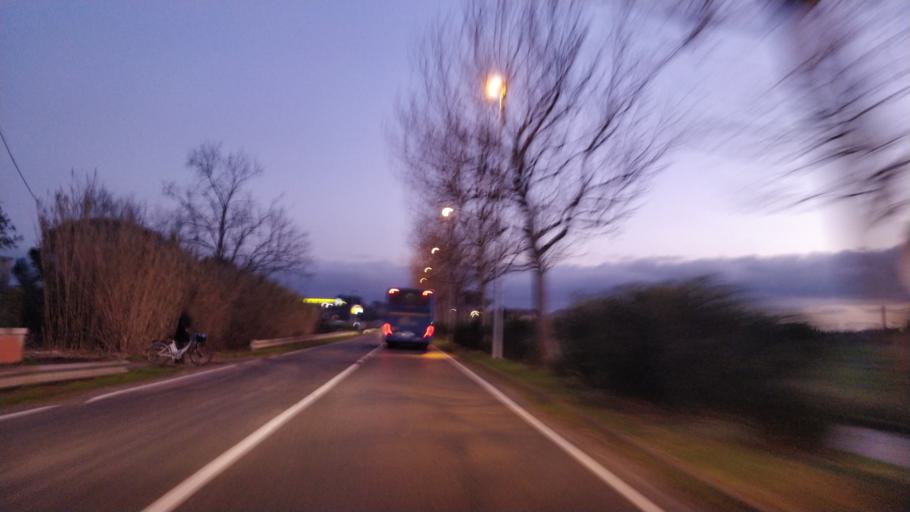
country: IT
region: Tuscany
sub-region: Provincia di Livorno
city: S.P. in Palazzi
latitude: 43.3207
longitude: 10.5115
